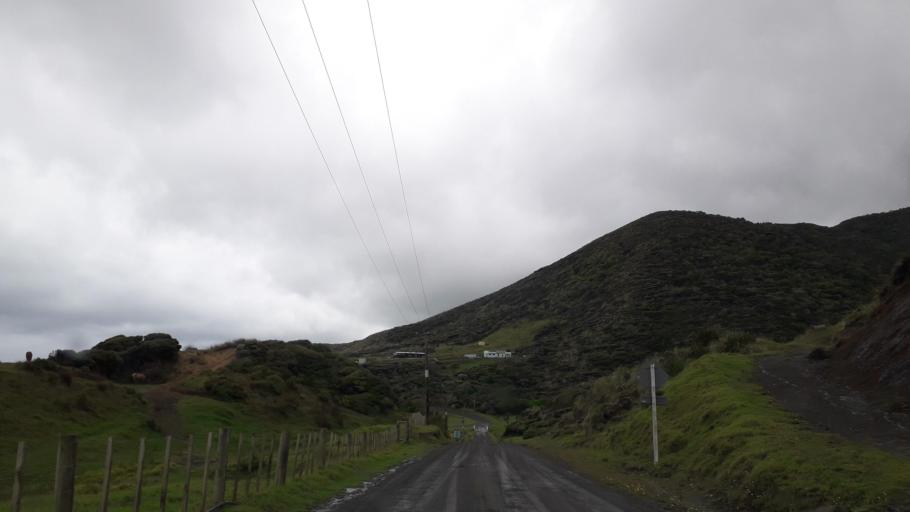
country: NZ
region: Northland
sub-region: Far North District
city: Ahipara
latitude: -35.4357
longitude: 173.2837
